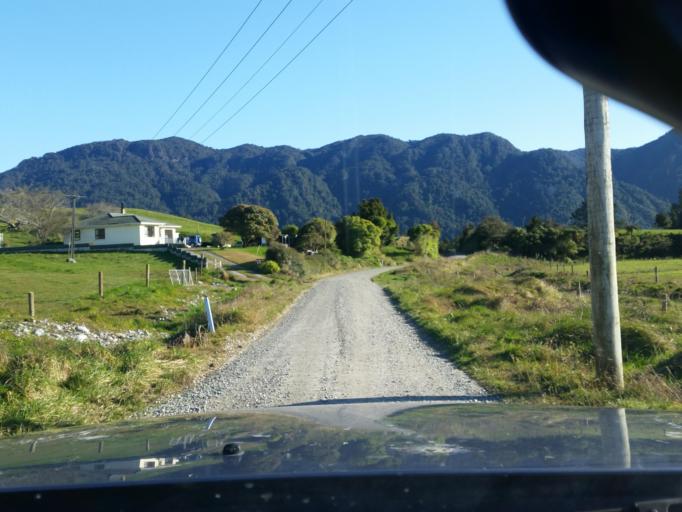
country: NZ
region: Tasman
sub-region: Tasman District
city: Takaka
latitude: -40.6869
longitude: 172.6504
